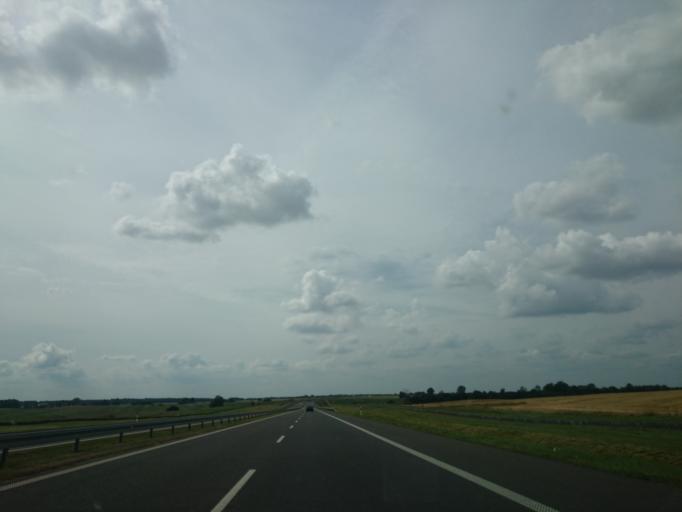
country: PL
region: West Pomeranian Voivodeship
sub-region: Powiat pyrzycki
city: Kozielice
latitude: 53.0999
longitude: 14.7947
